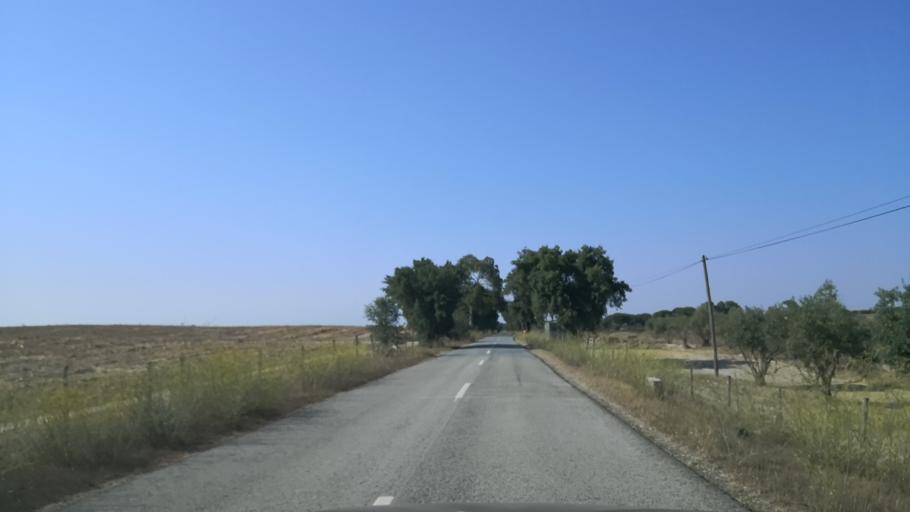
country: PT
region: Evora
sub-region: Vendas Novas
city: Vendas Novas
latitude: 38.7288
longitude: -8.6226
